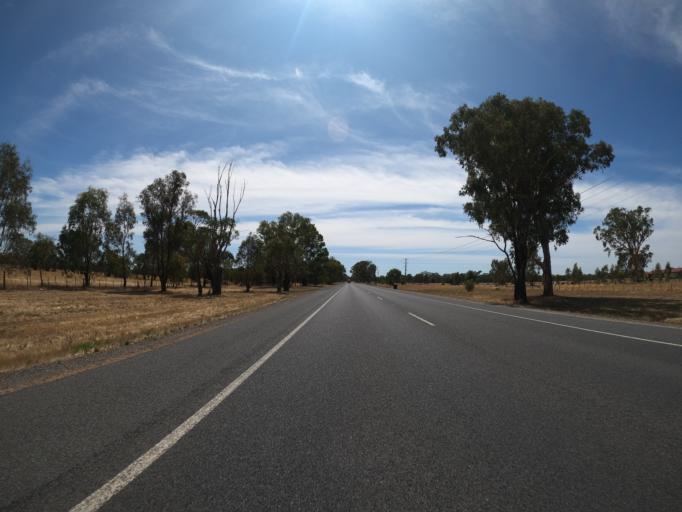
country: AU
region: Victoria
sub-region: Benalla
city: Benalla
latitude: -36.5261
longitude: 146.0506
